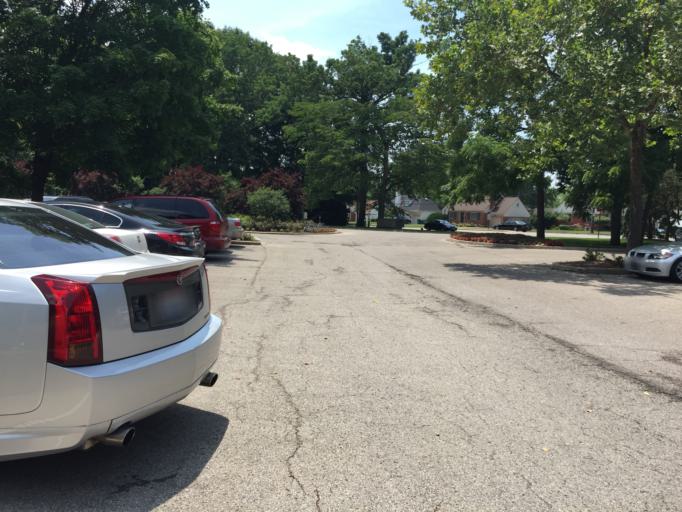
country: US
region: Ohio
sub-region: Montgomery County
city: Kettering
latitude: 39.6963
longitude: -84.1623
